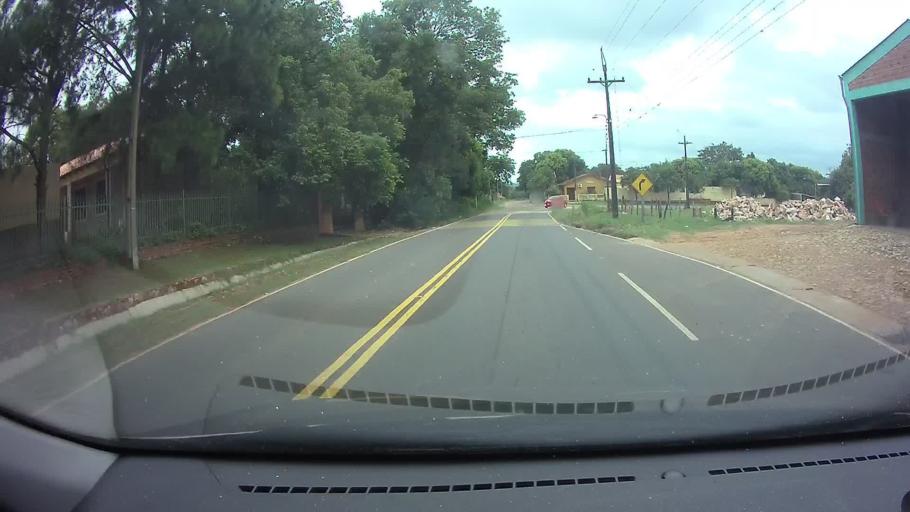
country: PY
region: Central
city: Nueva Italia
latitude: -25.6043
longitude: -57.4150
